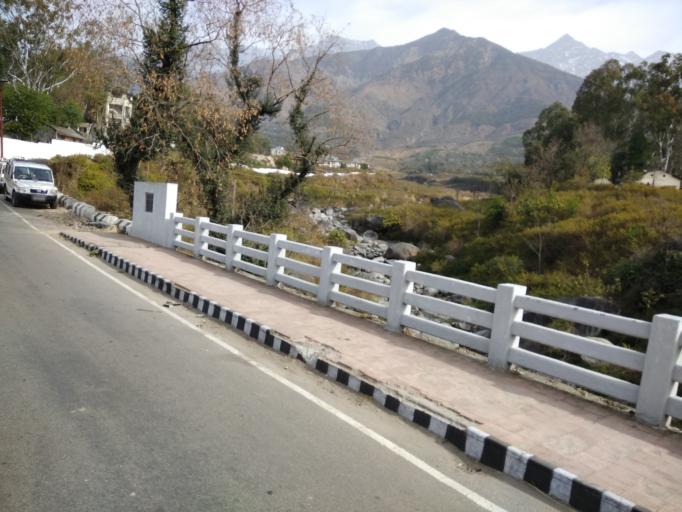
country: IN
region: Himachal Pradesh
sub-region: Kangra
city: Dharmsala
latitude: 32.1723
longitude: 76.3863
